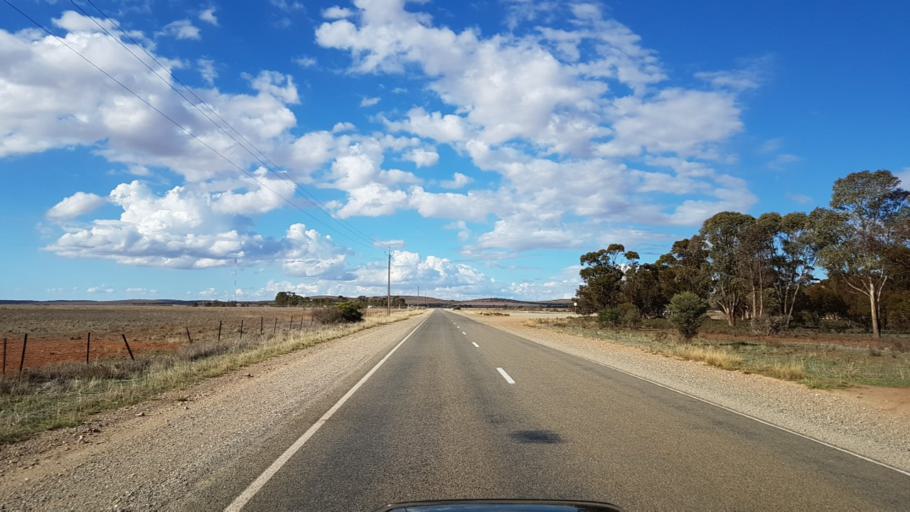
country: AU
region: South Australia
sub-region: Peterborough
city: Peterborough
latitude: -32.9696
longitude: 138.8614
